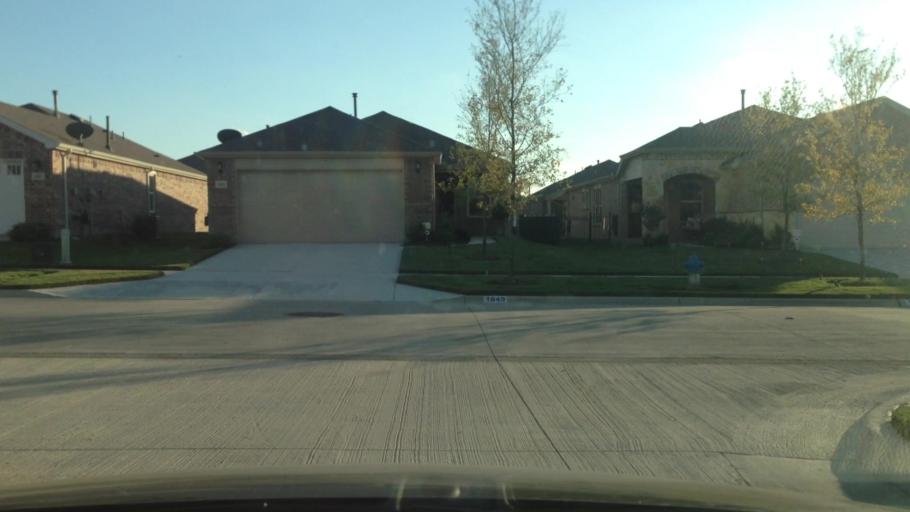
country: US
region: Texas
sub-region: Denton County
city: Little Elm
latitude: 33.1453
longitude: -96.9087
